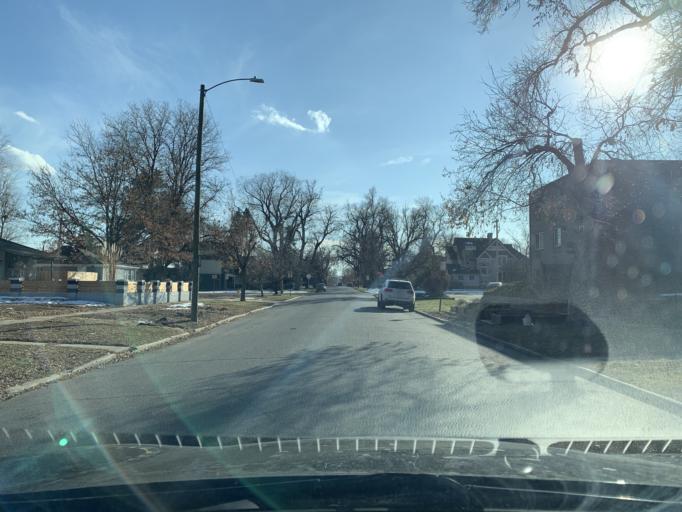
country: US
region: Colorado
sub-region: Jefferson County
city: Edgewater
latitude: 39.7507
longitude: -105.0269
